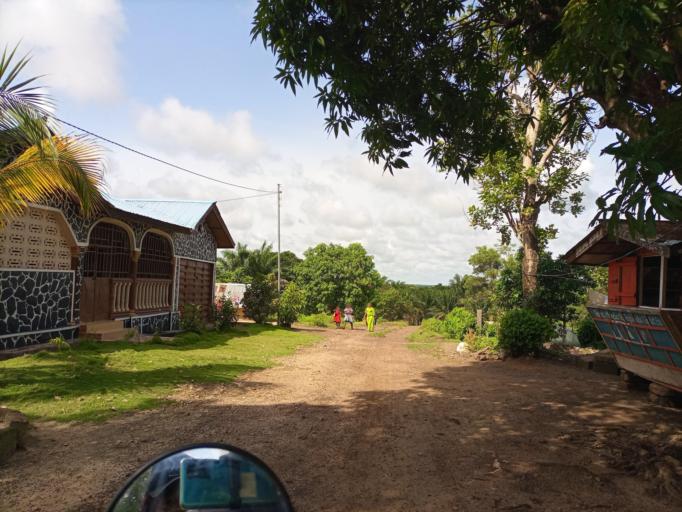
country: SL
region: Southern Province
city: Bo
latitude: 7.9655
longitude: -11.7652
